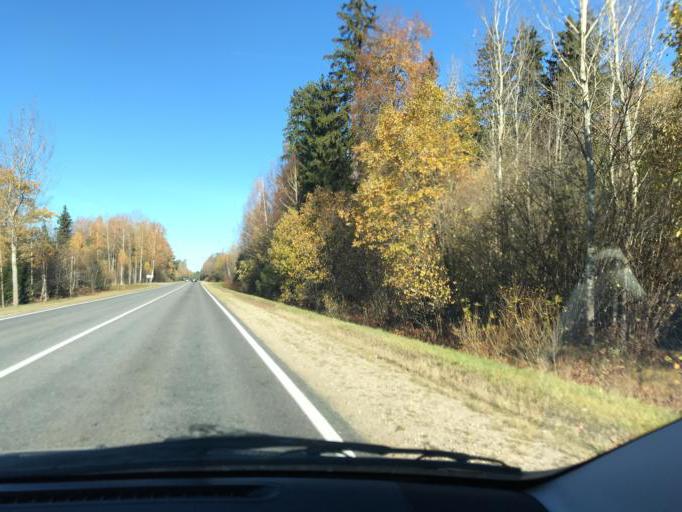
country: BY
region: Vitebsk
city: Lyepyel'
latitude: 54.9834
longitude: 28.7428
